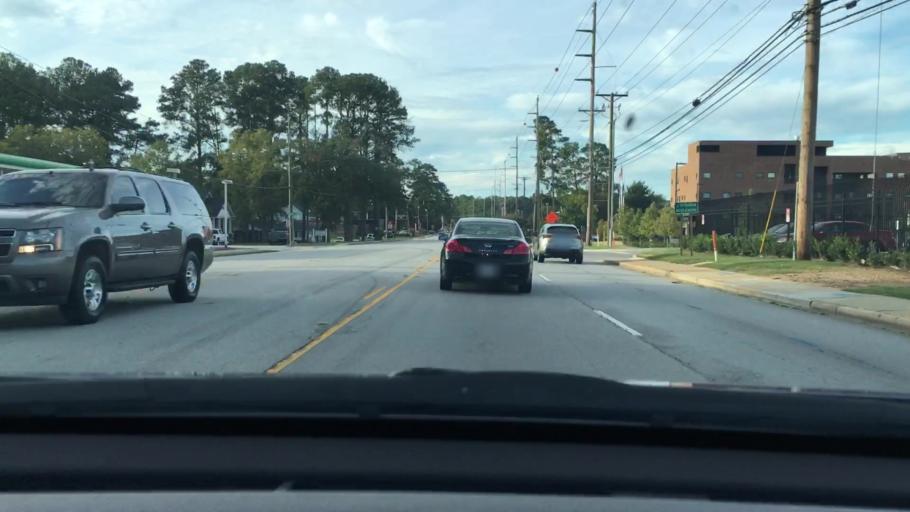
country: US
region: South Carolina
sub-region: Lexington County
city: Saint Andrews
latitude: 34.0652
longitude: -81.1162
